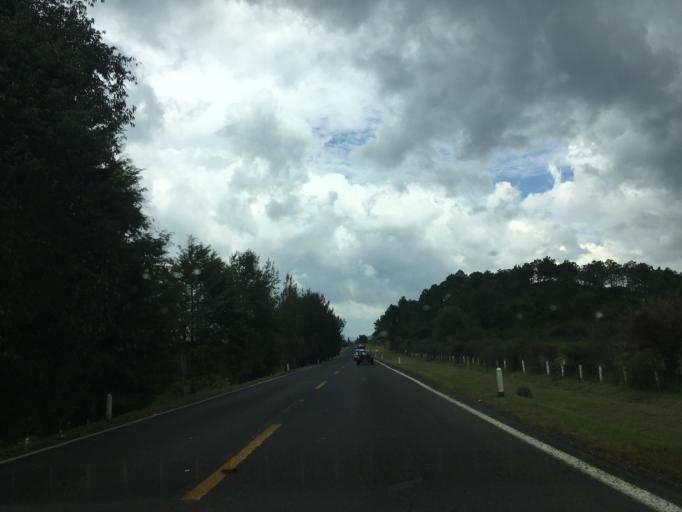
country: MX
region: Michoacan
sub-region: Patzcuaro
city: Santa Ana Chapitiro
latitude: 19.5310
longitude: -101.6375
